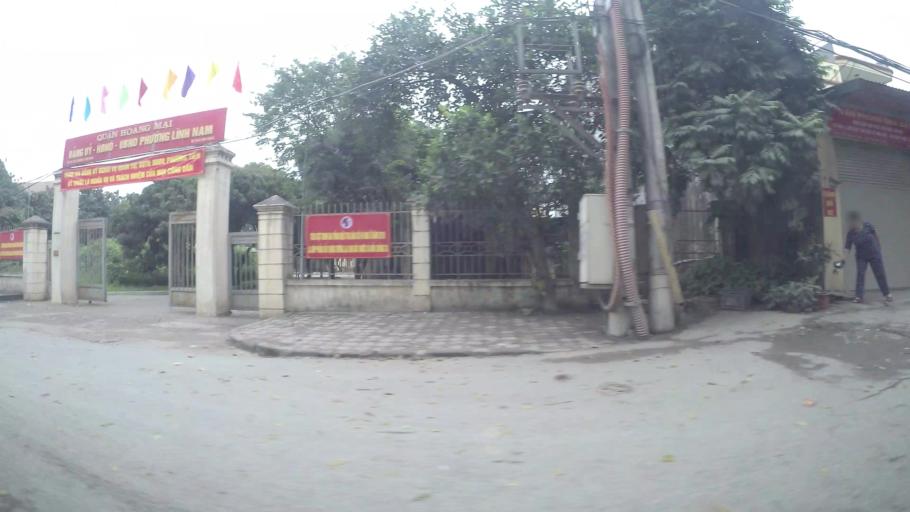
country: VN
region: Ha Noi
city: Hai BaTrung
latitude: 20.9794
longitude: 105.8903
